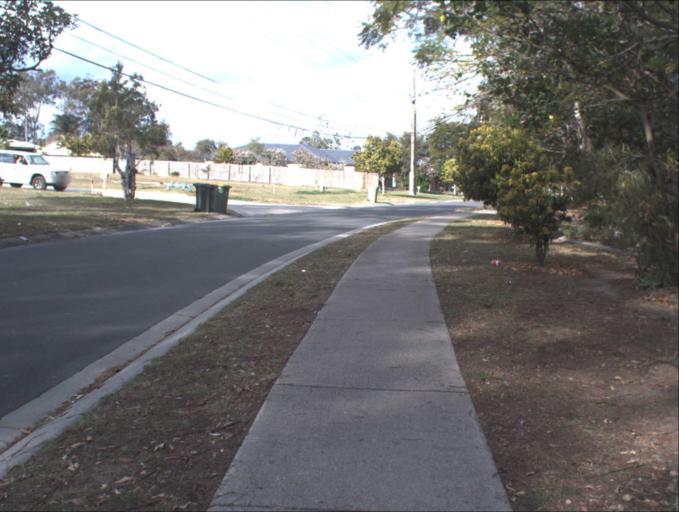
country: AU
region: Queensland
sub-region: Logan
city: Waterford West
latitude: -27.6789
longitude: 153.1255
